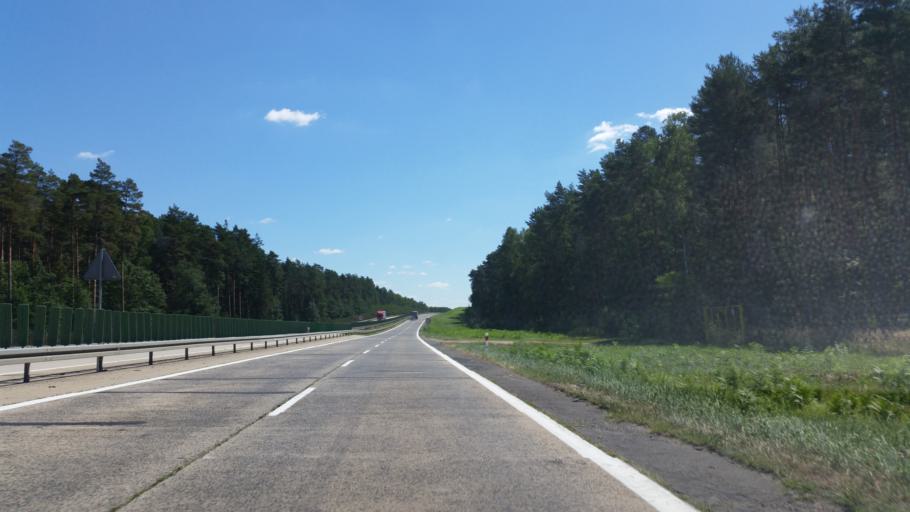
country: PL
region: Lubusz
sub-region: Powiat zaganski
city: Malomice
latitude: 51.4148
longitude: 15.4897
